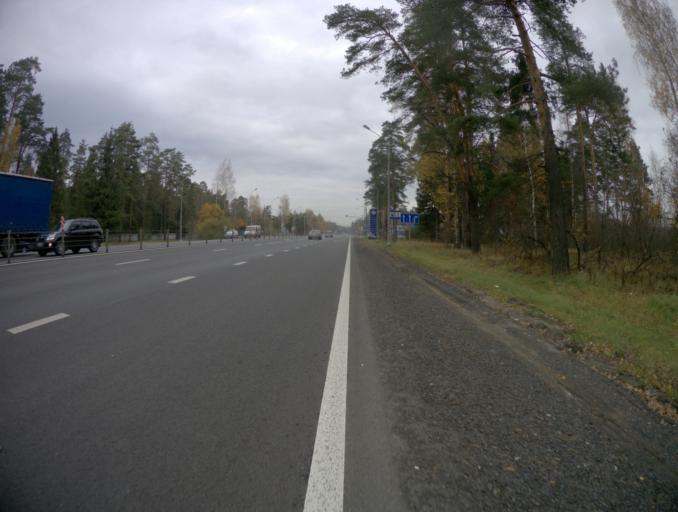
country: RU
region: Moskovskaya
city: Malaya Dubna
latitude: 55.8474
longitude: 38.9647
